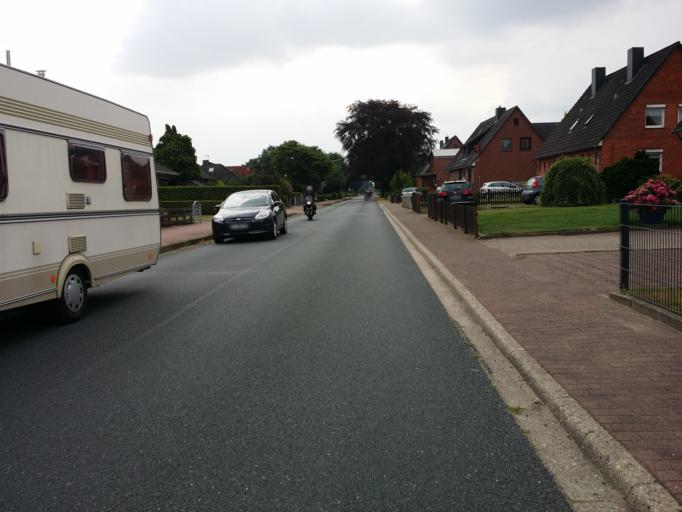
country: DE
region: Schleswig-Holstein
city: Krempermoor
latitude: 53.8761
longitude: 9.4810
